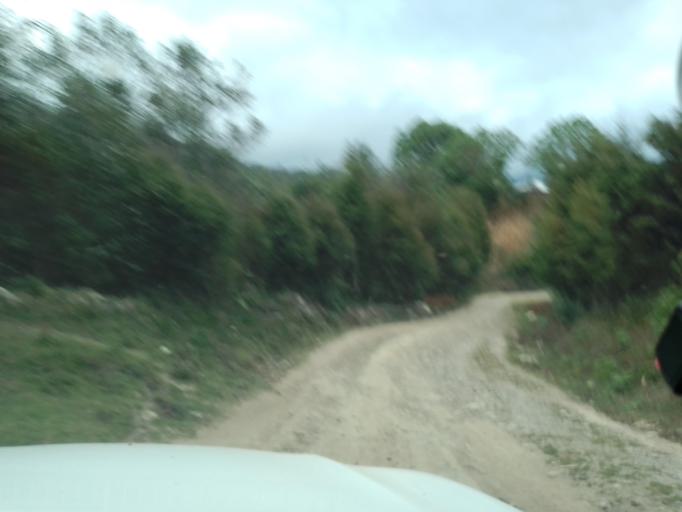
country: MX
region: Chiapas
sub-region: Cacahoatan
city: Benito Juarez
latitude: 15.2071
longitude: -92.2188
